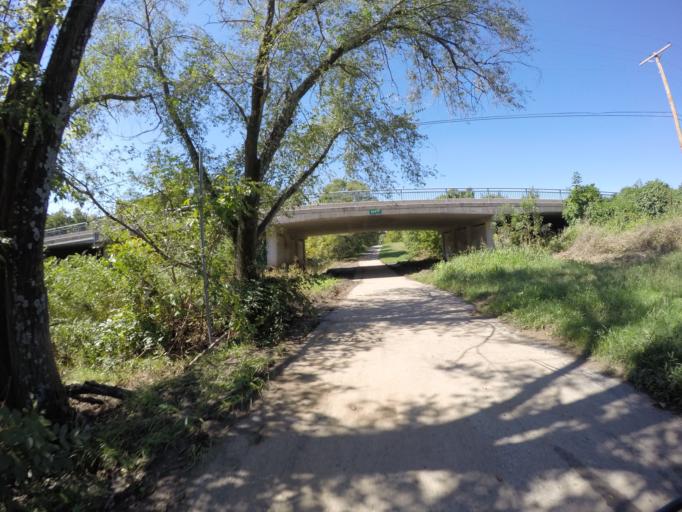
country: US
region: Kansas
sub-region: Johnson County
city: Overland Park
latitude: 38.9410
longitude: -94.6709
